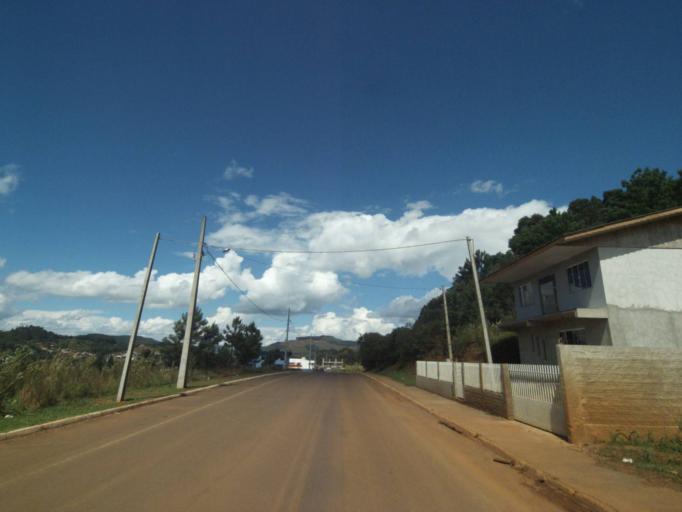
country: BR
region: Parana
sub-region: Uniao Da Vitoria
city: Uniao da Vitoria
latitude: -26.1540
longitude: -51.5490
